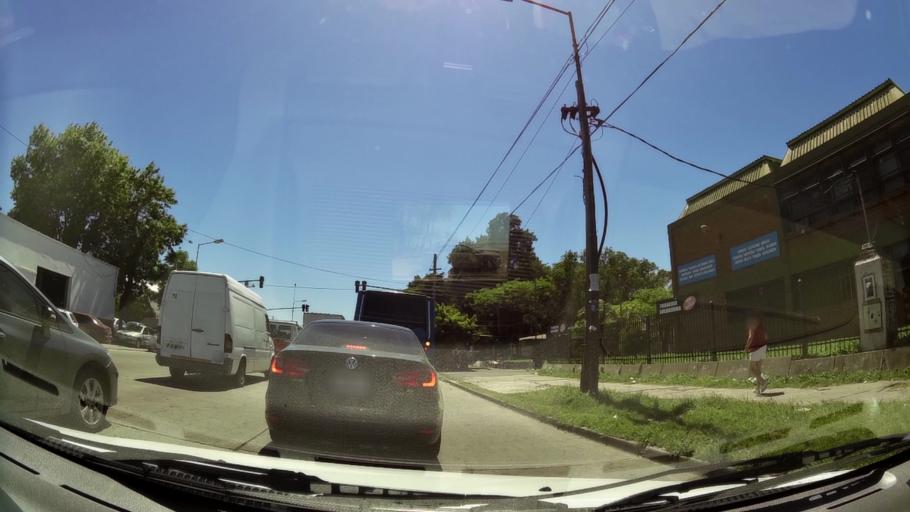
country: AR
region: Buenos Aires
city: Caseros
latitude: -34.5816
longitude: -58.5545
